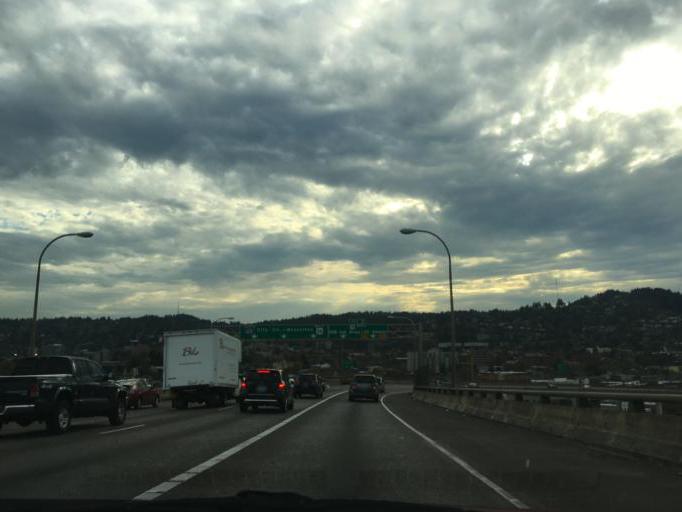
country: US
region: Oregon
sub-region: Multnomah County
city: Portland
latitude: 45.5358
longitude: -122.6857
